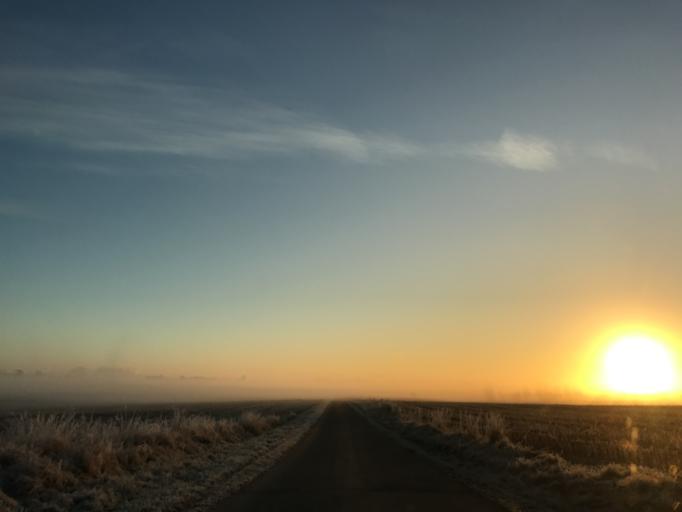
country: DK
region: South Denmark
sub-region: Haderslev Kommune
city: Haderslev
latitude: 55.2063
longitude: 9.4914
